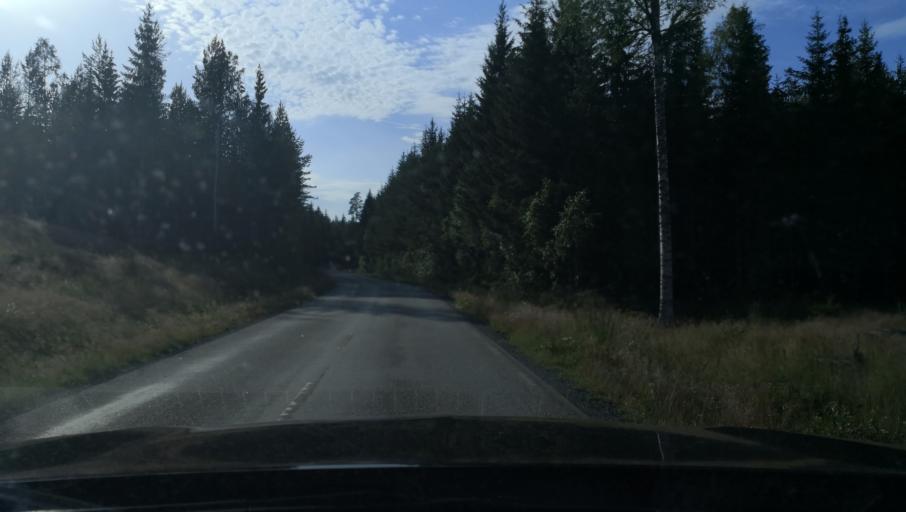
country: SE
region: Dalarna
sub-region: Smedjebackens Kommun
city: Smedjebacken
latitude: 59.9785
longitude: 15.3929
